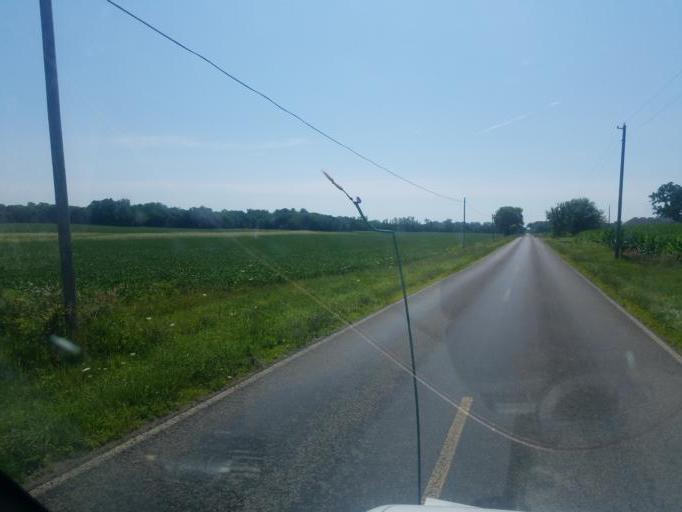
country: US
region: Ohio
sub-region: Champaign County
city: North Lewisburg
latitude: 40.2153
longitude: -83.5073
